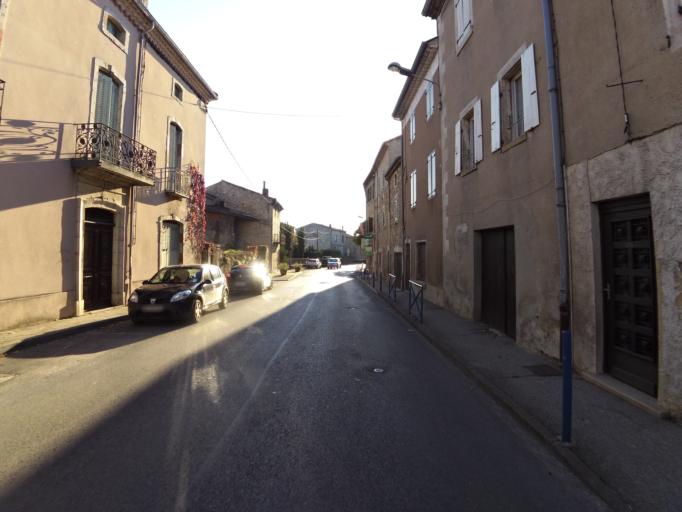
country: FR
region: Rhone-Alpes
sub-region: Departement de l'Ardeche
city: Rosieres
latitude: 44.4835
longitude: 4.2572
